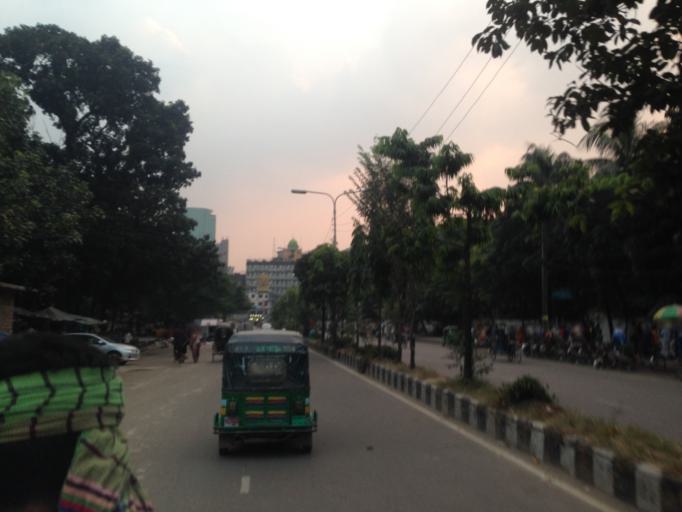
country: BD
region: Dhaka
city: Paltan
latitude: 23.7343
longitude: 90.4213
